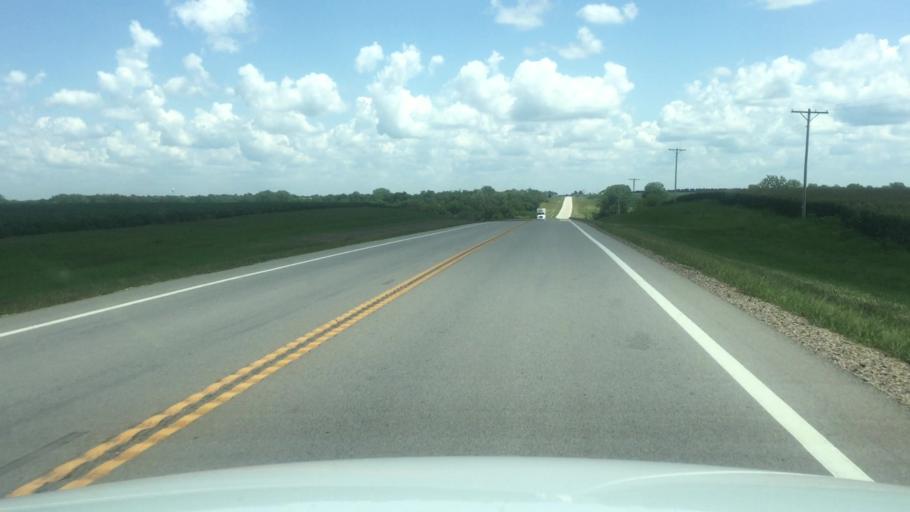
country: US
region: Kansas
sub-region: Brown County
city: Horton
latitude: 39.6673
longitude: -95.4584
